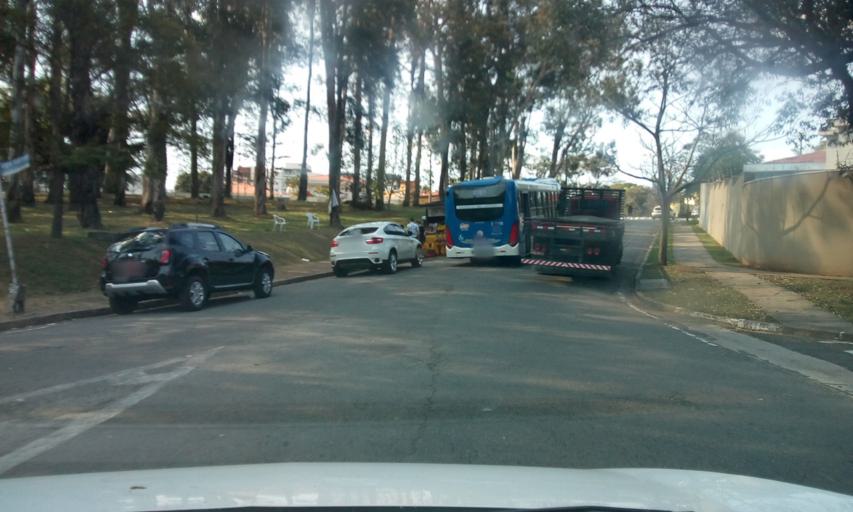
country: BR
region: Sao Paulo
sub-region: Osasco
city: Osasco
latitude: -23.5256
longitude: -46.7241
